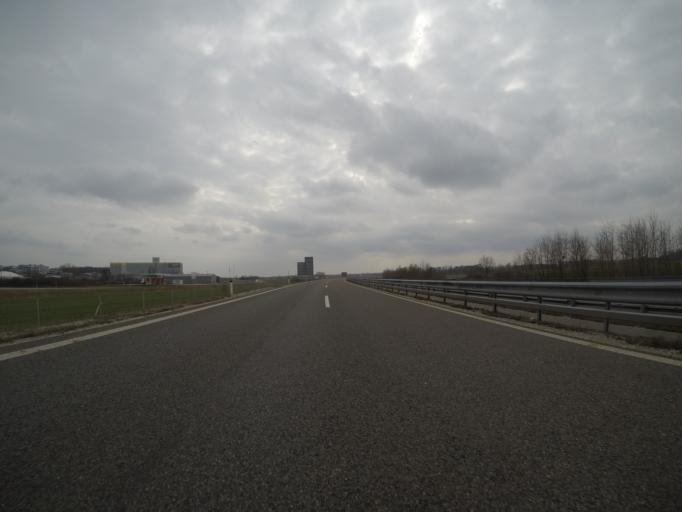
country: SI
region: Lendava-Lendva
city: Lendava
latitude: 46.5497
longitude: 16.4441
